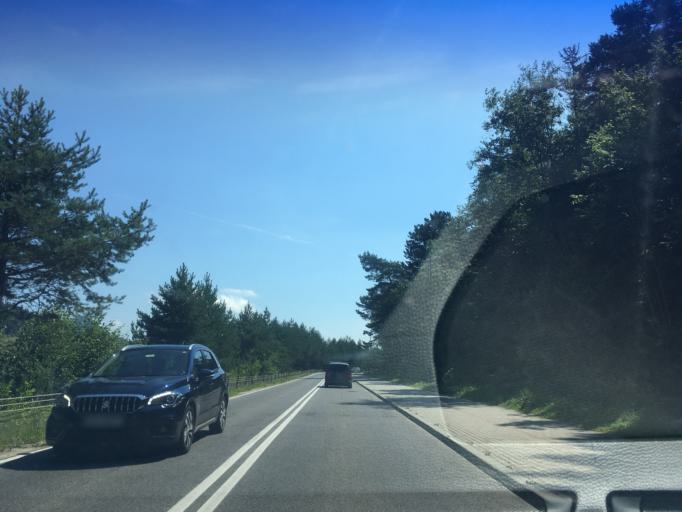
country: PL
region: Lesser Poland Voivodeship
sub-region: Powiat nowotarski
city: Niedzica
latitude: 49.4066
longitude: 20.3266
